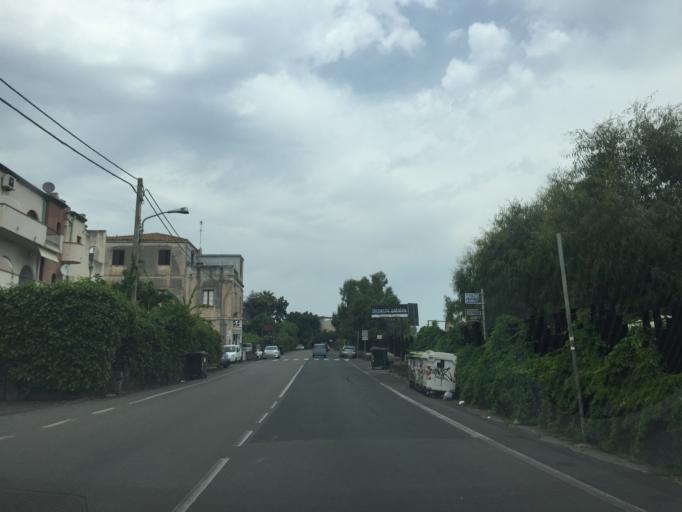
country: IT
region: Sicily
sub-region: Catania
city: Vambolieri
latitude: 37.5729
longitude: 15.1662
